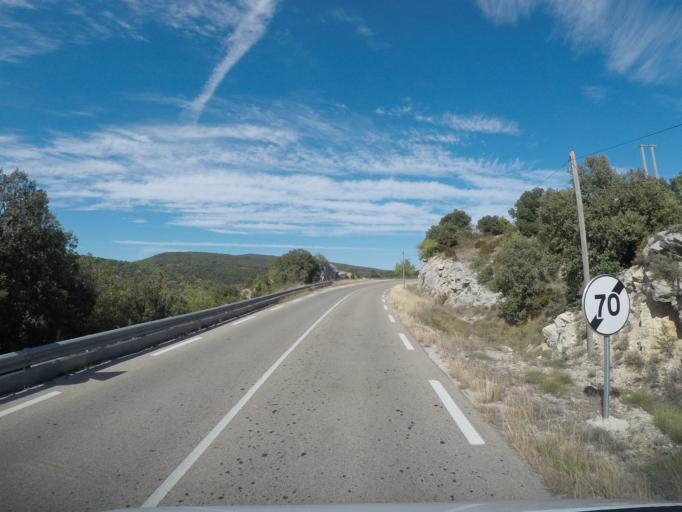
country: FR
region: Languedoc-Roussillon
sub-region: Departement de l'Herault
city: Saint-Martin-de-Londres
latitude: 43.8150
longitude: 3.7435
